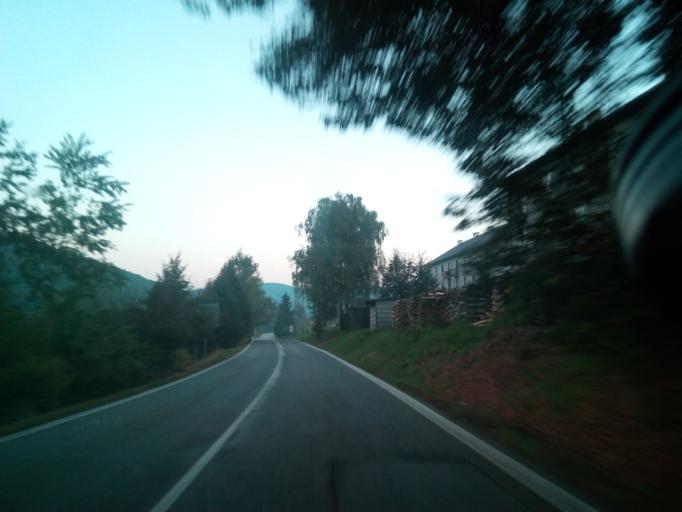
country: SK
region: Kosicky
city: Dobsina
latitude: 48.7462
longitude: 20.4158
